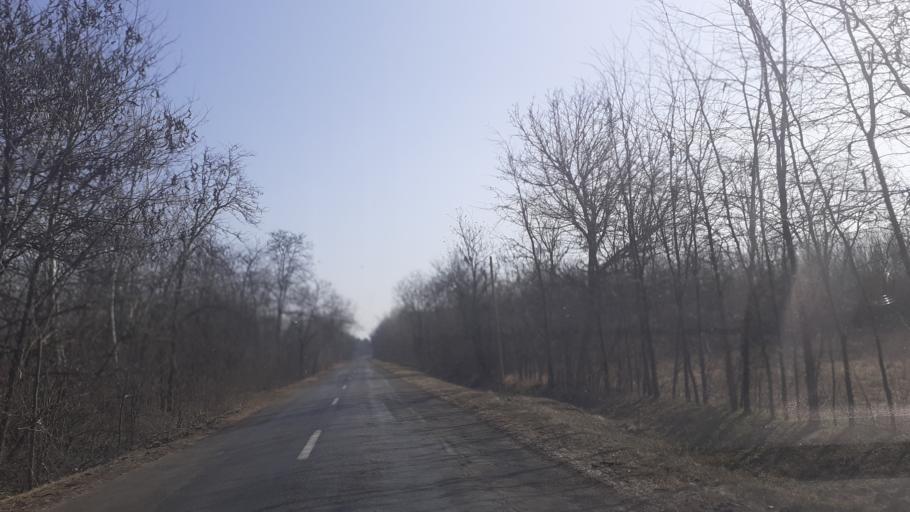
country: HU
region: Pest
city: Orkeny
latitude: 47.0636
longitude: 19.3984
